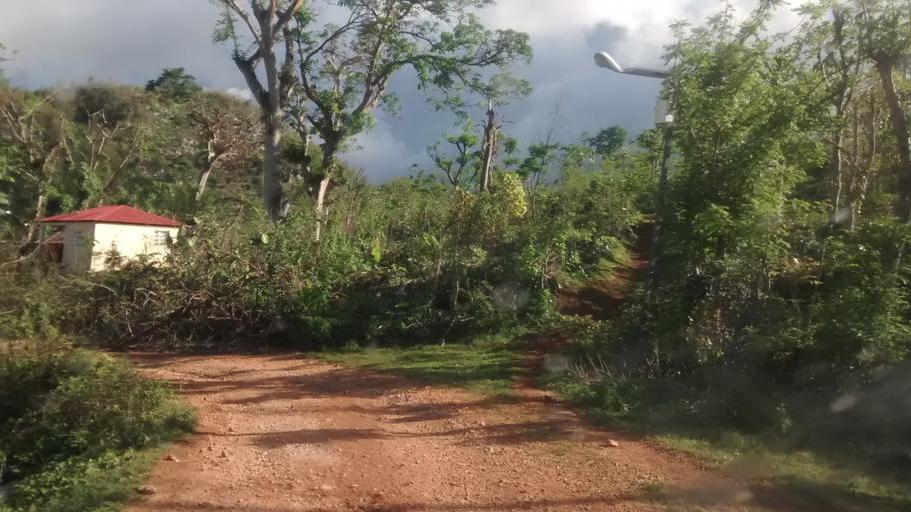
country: HT
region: Grandans
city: Corail
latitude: 18.5310
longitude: -73.8460
